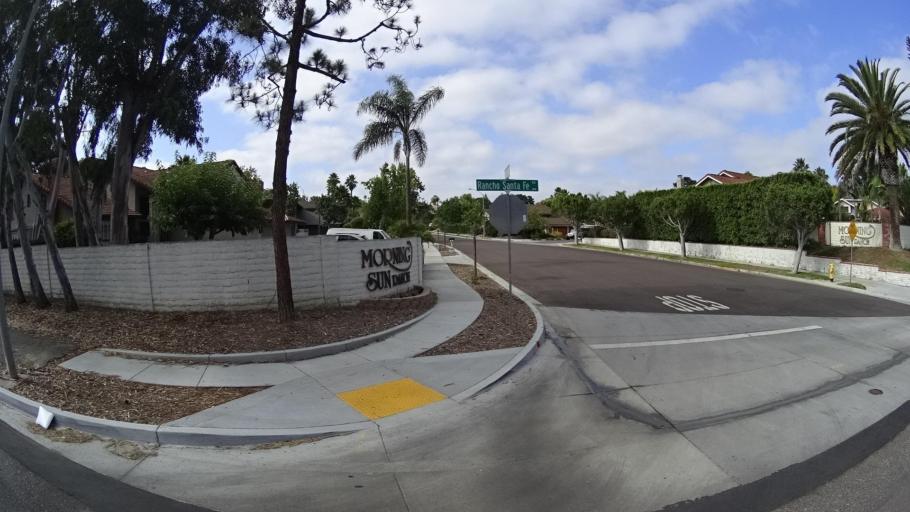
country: US
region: California
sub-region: San Diego County
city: Rancho Santa Fe
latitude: 33.0596
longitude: -117.2379
